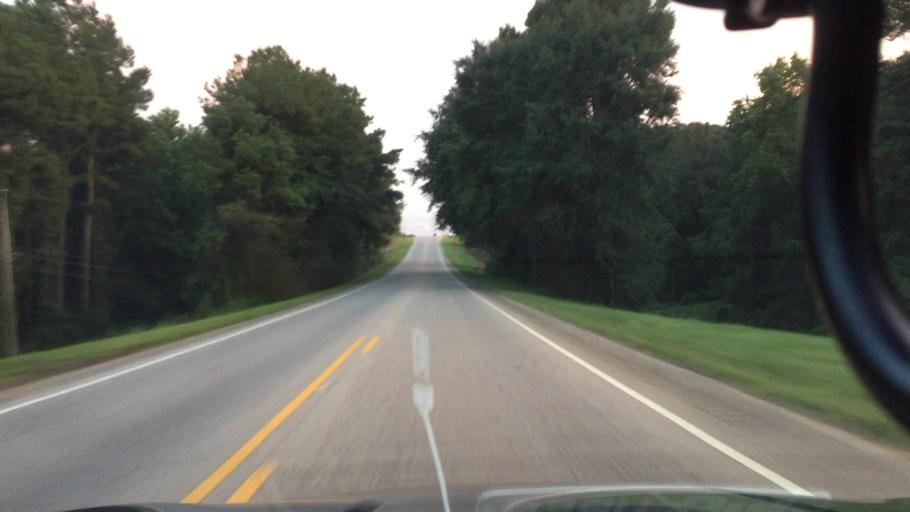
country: US
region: Alabama
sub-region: Coffee County
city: Enterprise
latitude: 31.3650
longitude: -85.8683
